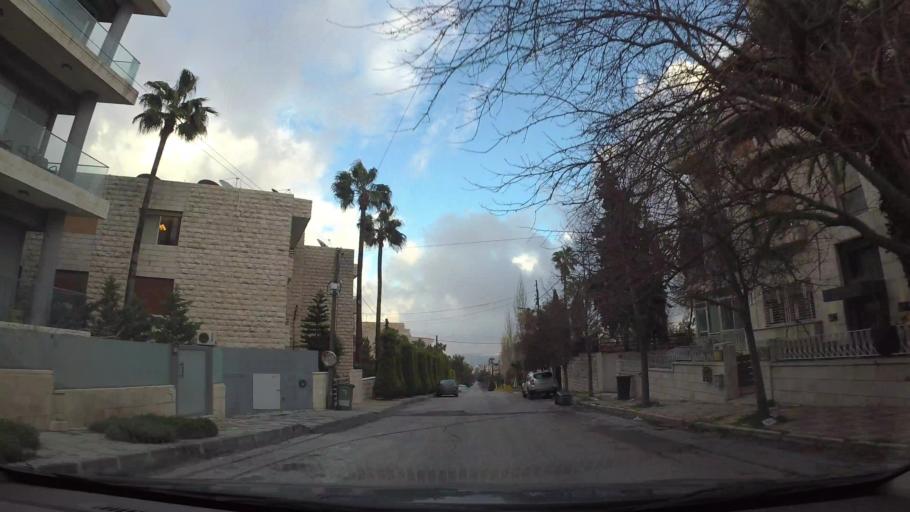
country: JO
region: Amman
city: Amman
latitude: 31.9568
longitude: 35.8857
